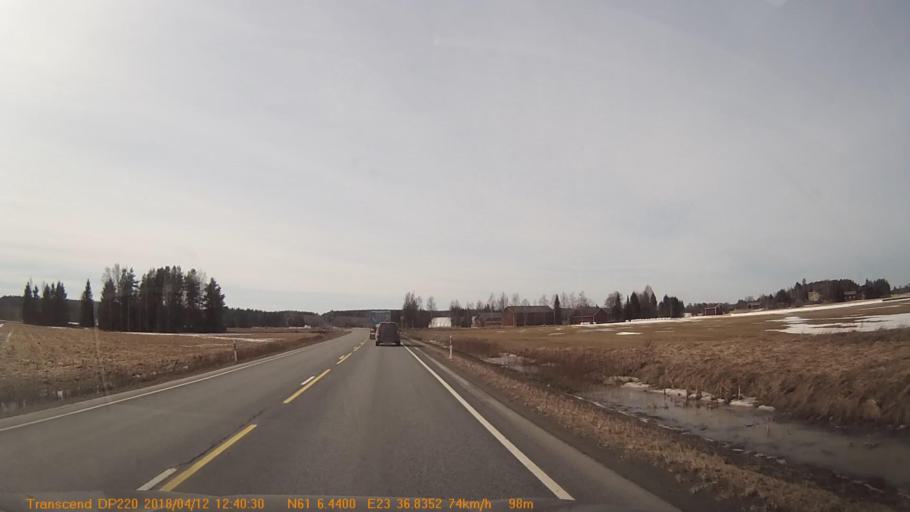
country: FI
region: Pirkanmaa
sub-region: Etelae-Pirkanmaa
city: Urjala
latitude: 61.1075
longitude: 23.6142
